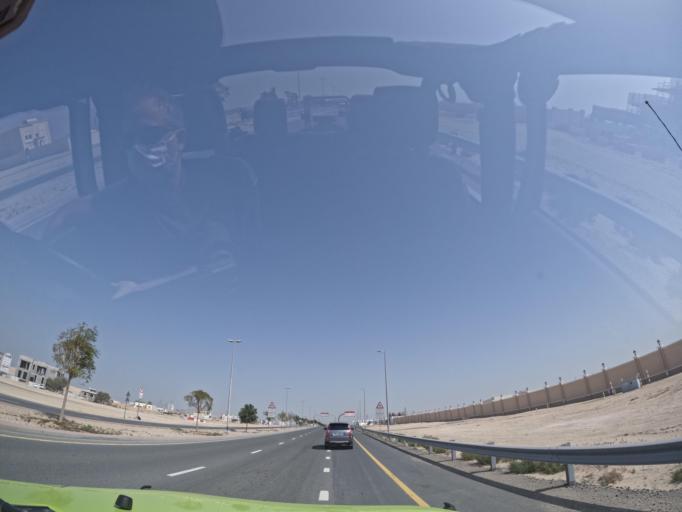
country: AE
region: Ash Shariqah
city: Sharjah
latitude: 25.1549
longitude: 55.3626
